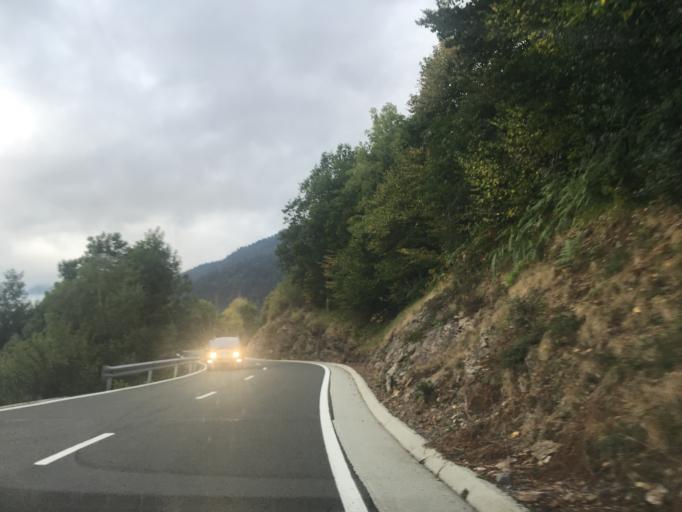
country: ES
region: Catalonia
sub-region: Provincia de Lleida
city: Les
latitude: 42.7736
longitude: 0.6777
